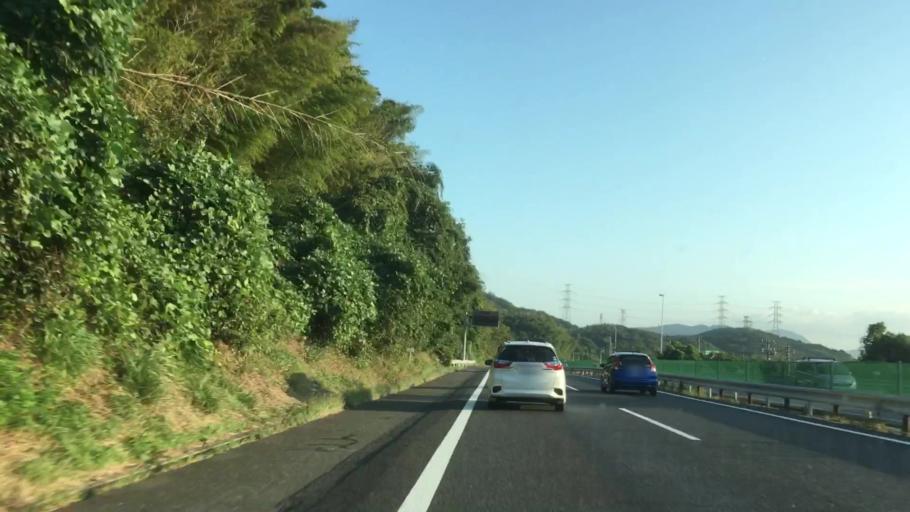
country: JP
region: Yamaguchi
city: Shimonoseki
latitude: 33.9844
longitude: 130.9516
